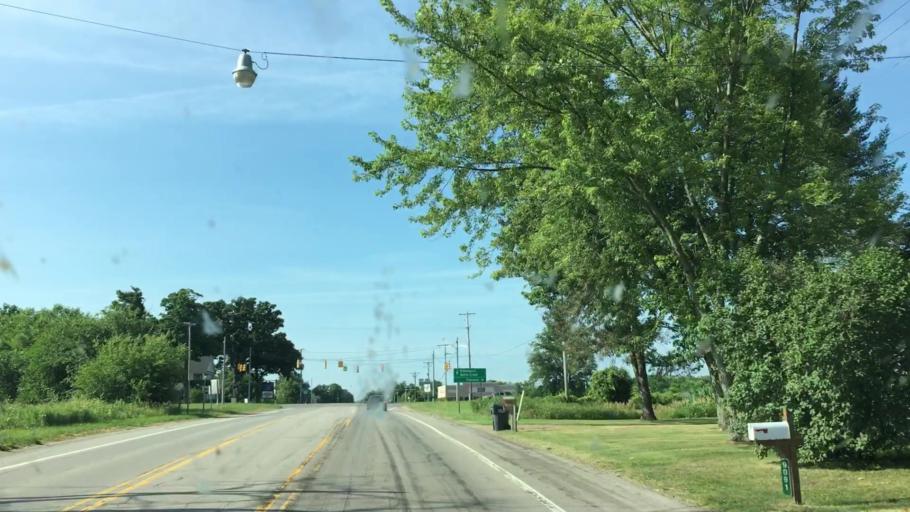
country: US
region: Michigan
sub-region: Kalamazoo County
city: South Gull Lake
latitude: 42.3919
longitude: -85.4553
